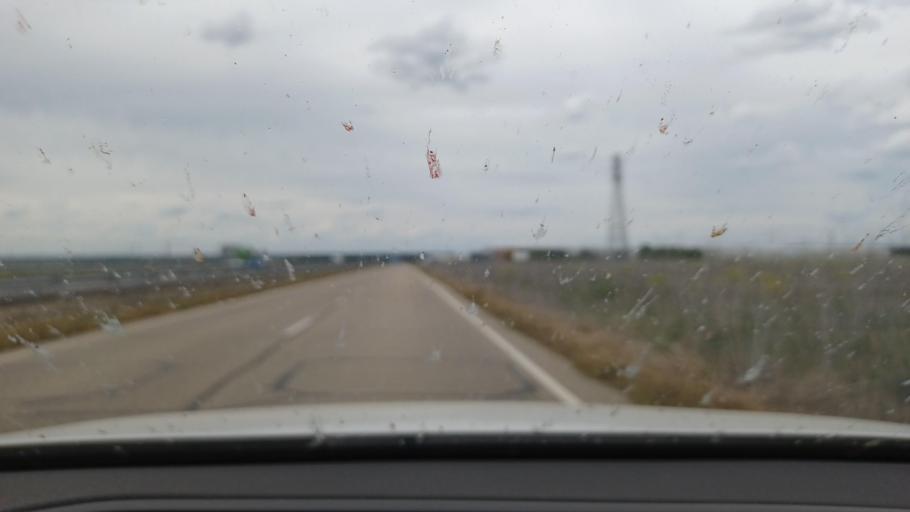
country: ES
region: Castille and Leon
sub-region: Provincia de Valladolid
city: Aldeamayor de San Martin
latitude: 41.4955
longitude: -4.6178
